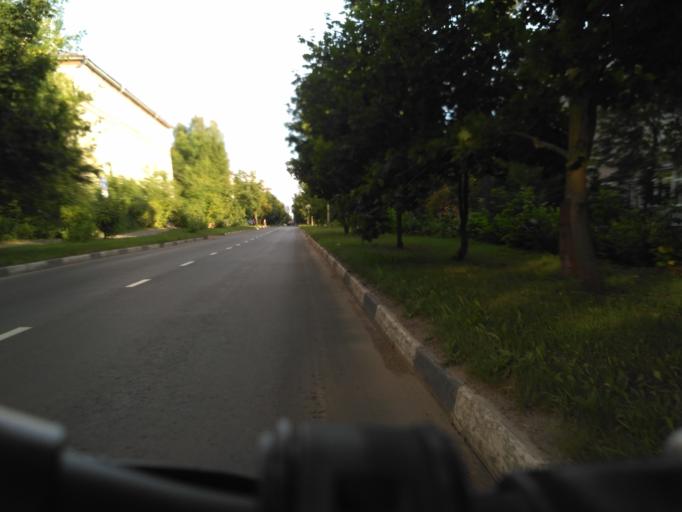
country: RU
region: Moskovskaya
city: Dubna
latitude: 56.7521
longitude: 37.1979
